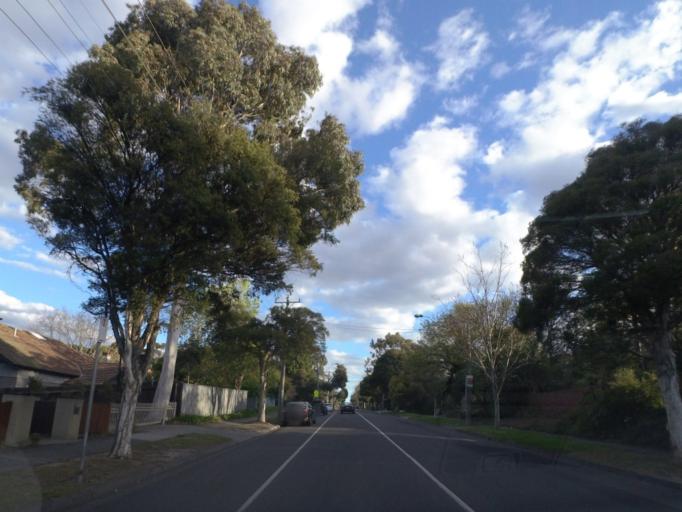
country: AU
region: Victoria
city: Mont Albert
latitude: -37.8097
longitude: 145.1004
